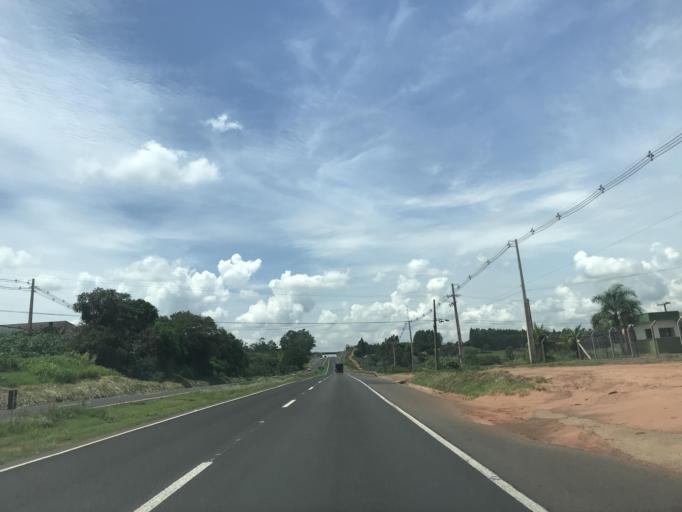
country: BR
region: Parana
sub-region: Alto Parana
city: Alto Parana
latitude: -23.1892
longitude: -52.2087
